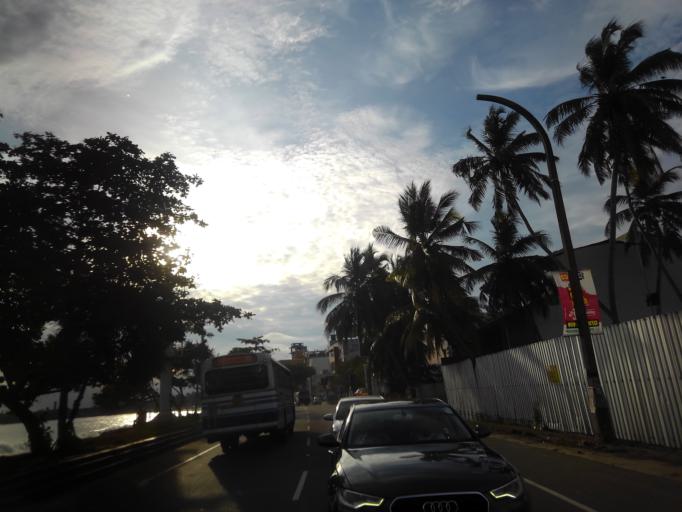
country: LK
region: Southern
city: Galle
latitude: 6.0371
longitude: 80.2249
